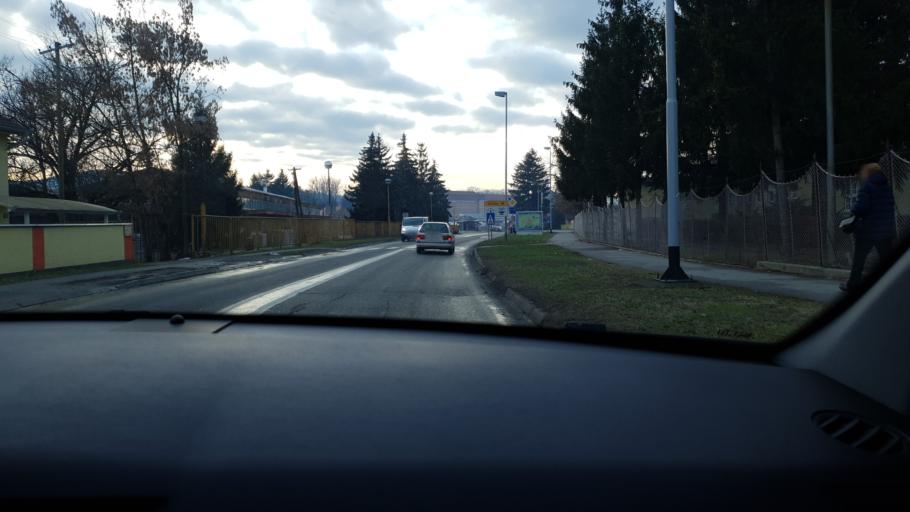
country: HR
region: Pozesko-Slavonska
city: Pozega
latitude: 45.3421
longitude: 17.6850
